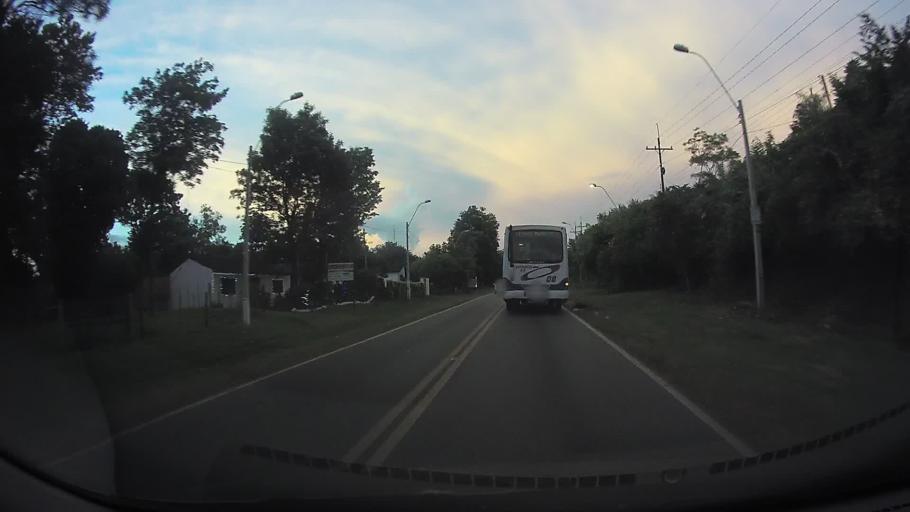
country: PY
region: Central
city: Ita
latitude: -25.4732
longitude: -57.3636
